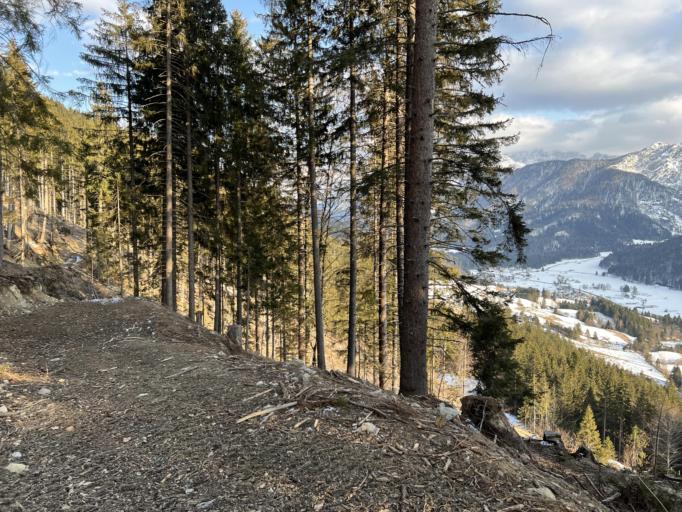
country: AT
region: Carinthia
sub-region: Politischer Bezirk Villach Land
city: Arnoldstein
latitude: 46.5077
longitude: 13.6973
